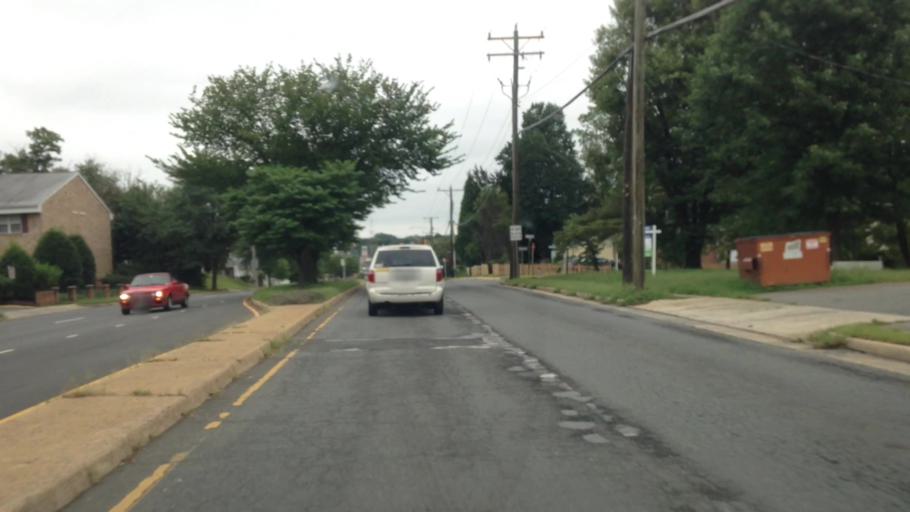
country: US
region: Virginia
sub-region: Fairfax County
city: Jefferson
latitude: 38.8788
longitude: -77.1862
